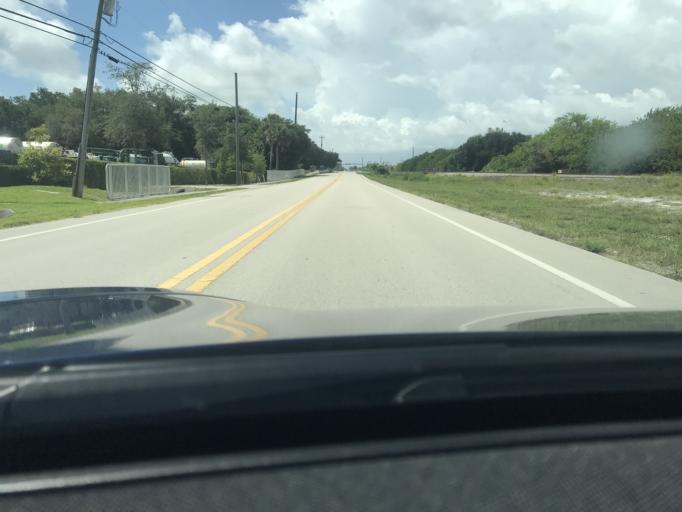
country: US
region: Florida
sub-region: Indian River County
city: Gifford
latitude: 27.6937
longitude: -80.4150
